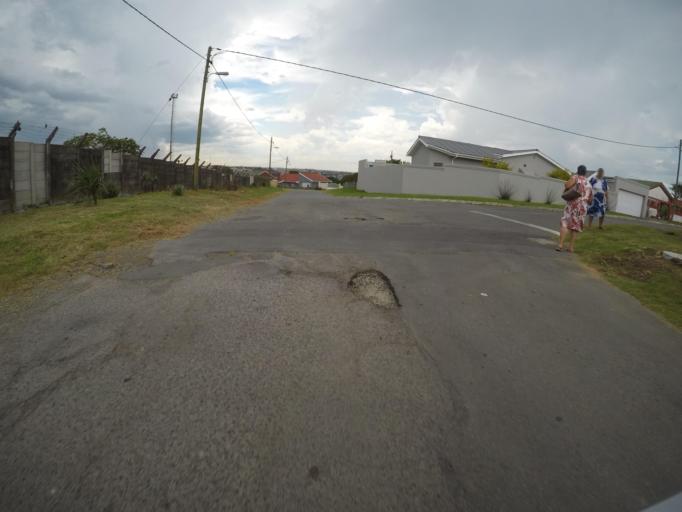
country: ZA
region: Eastern Cape
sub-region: Buffalo City Metropolitan Municipality
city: East London
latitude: -33.0244
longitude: 27.8642
